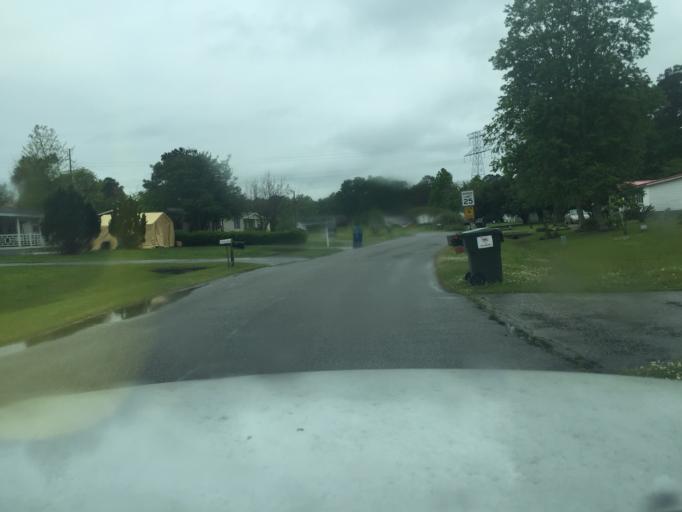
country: US
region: Georgia
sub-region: Chatham County
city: Georgetown
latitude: 32.0105
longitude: -81.2548
